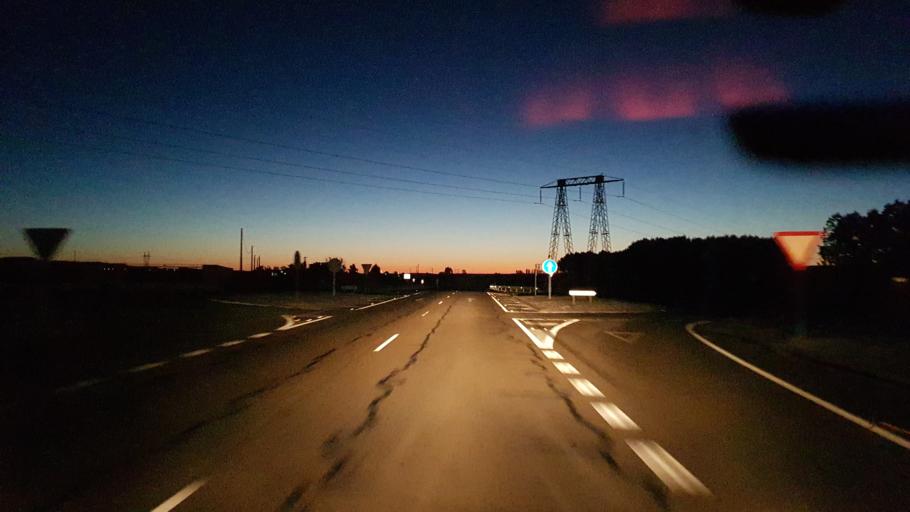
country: ES
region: Castille and Leon
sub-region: Provincia de Zamora
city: Monfarracinos
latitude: 41.5378
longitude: -5.7164
